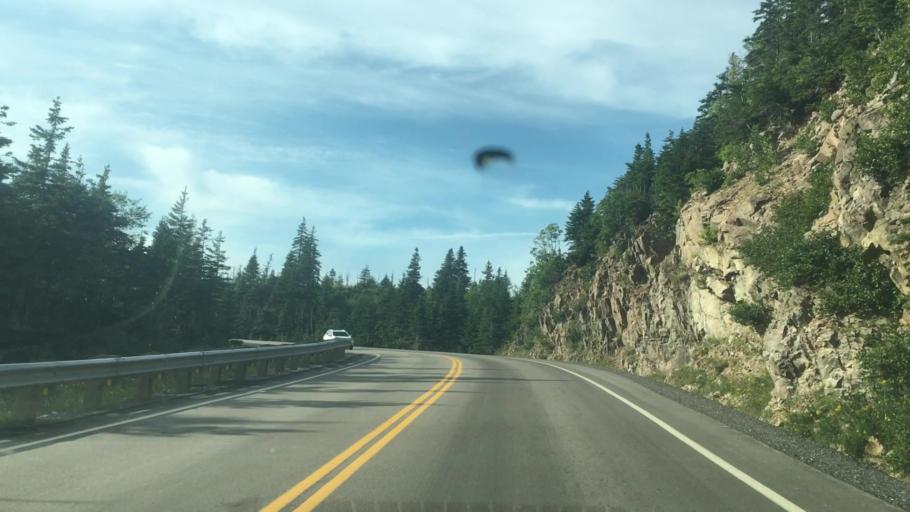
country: CA
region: Nova Scotia
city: Sydney Mines
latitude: 46.8231
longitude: -60.6553
